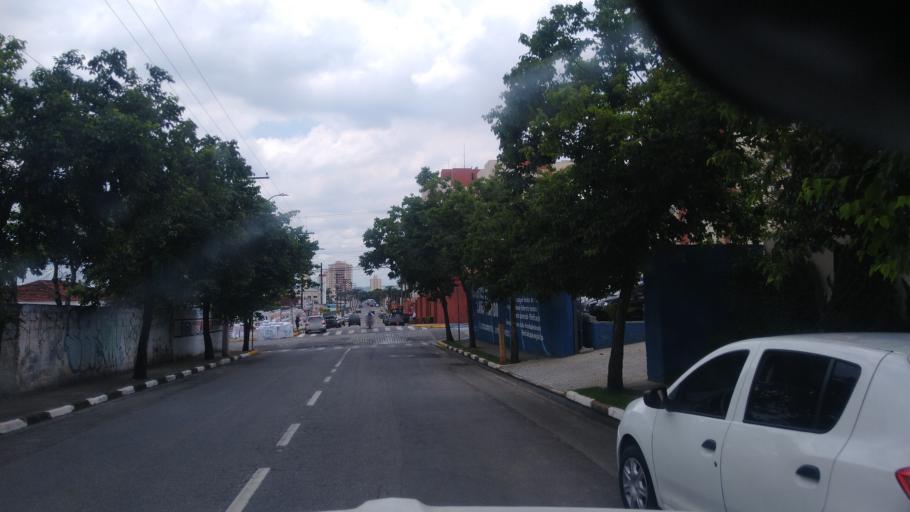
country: BR
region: Sao Paulo
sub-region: Suzano
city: Suzano
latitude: -23.5502
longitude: -46.3172
